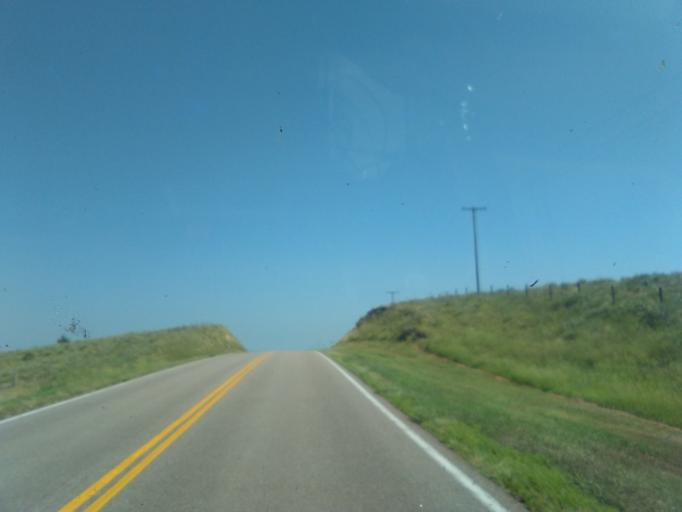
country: US
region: Nebraska
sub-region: Dundy County
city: Benkelman
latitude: 39.8694
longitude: -101.5412
